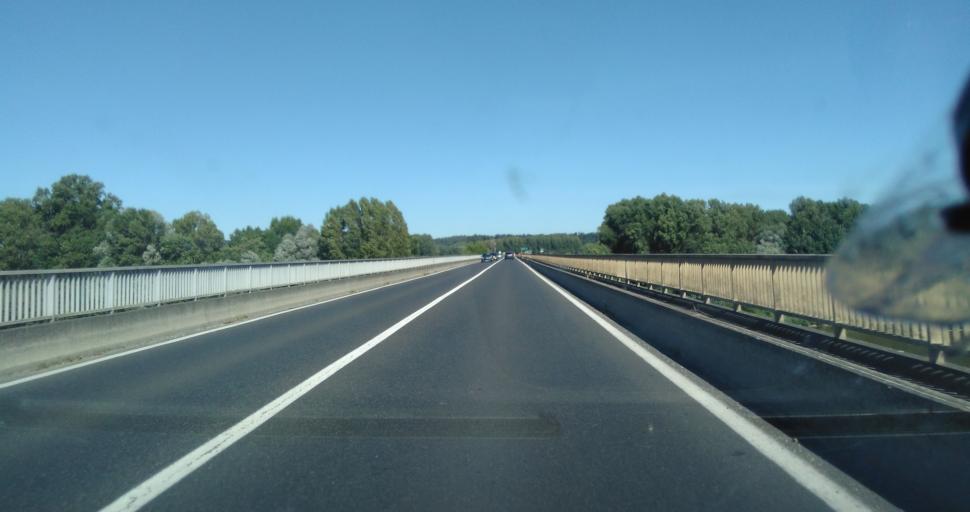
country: FR
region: Centre
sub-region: Departement d'Indre-et-Loire
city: Charge
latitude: 47.4282
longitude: 1.0095
